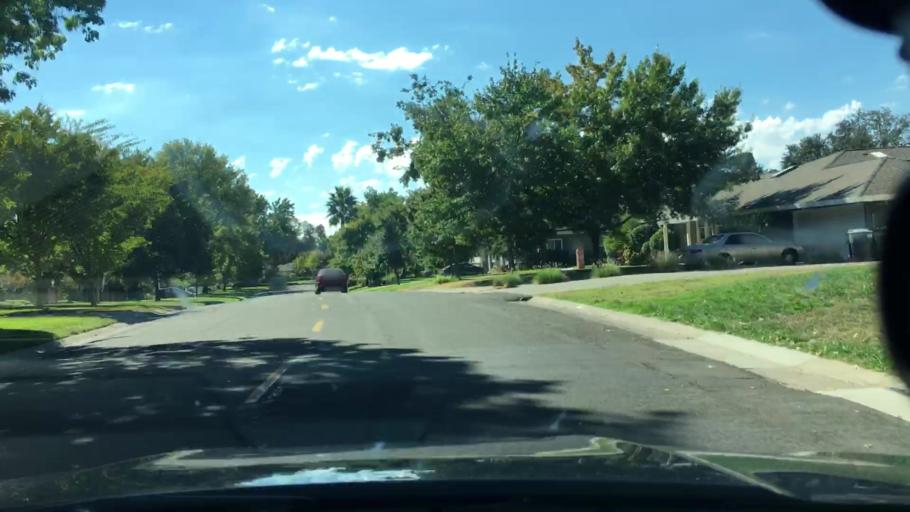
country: US
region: California
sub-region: Sacramento County
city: Arden-Arcade
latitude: 38.5786
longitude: -121.3803
